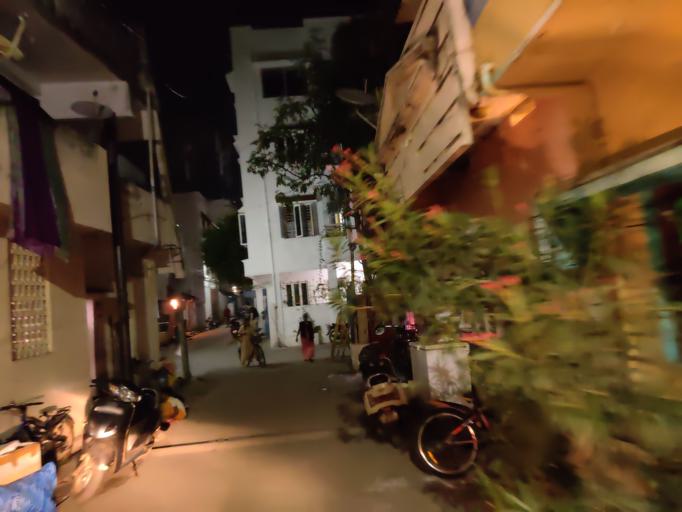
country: IN
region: Pondicherry
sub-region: Puducherry
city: Puducherry
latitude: 11.9448
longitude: 79.8363
